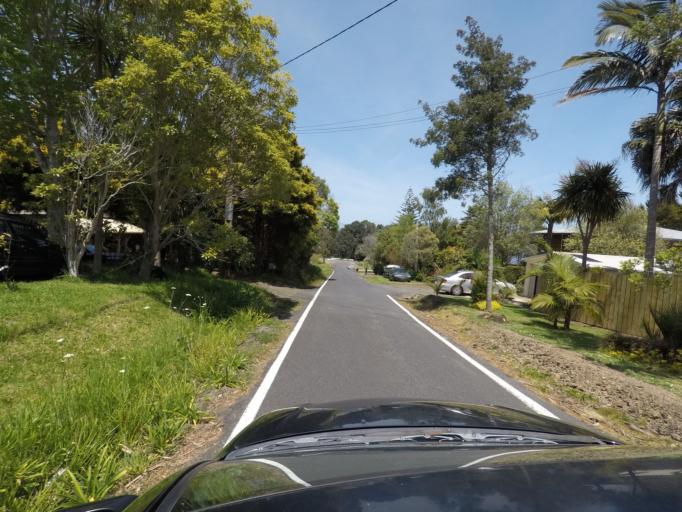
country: NZ
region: Auckland
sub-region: Auckland
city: Titirangi
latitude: -36.9780
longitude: 174.6319
